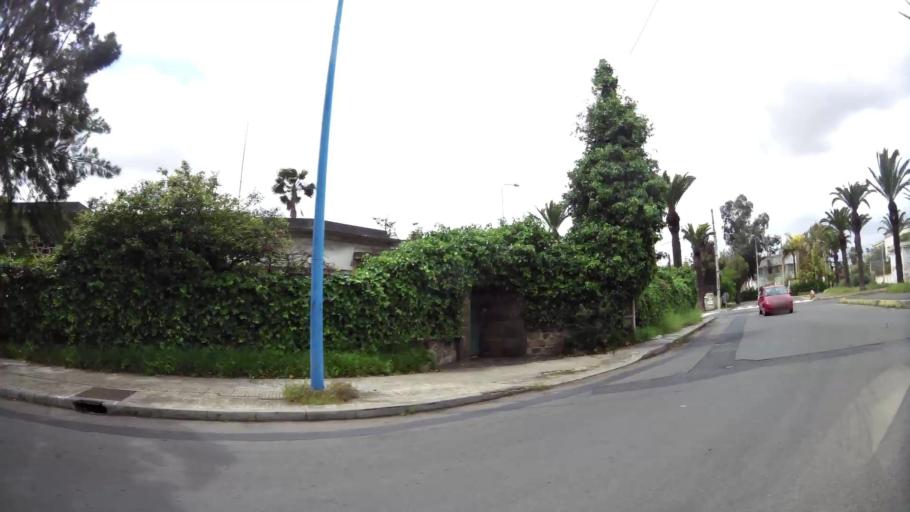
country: MA
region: Grand Casablanca
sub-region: Casablanca
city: Casablanca
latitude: 33.5600
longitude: -7.6178
